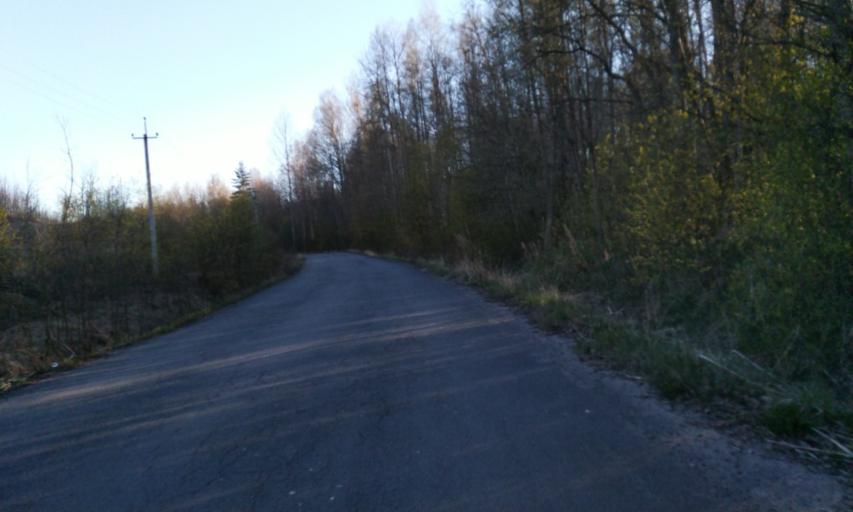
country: RU
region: Leningrad
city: Toksovo
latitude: 60.1424
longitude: 30.5713
